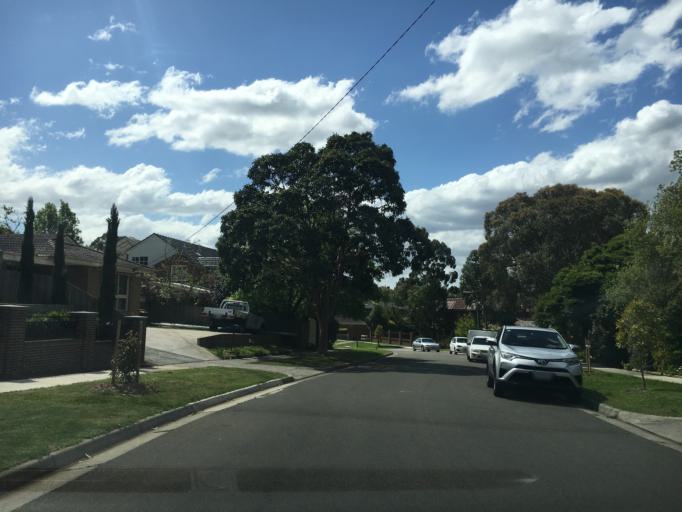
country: AU
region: Victoria
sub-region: Whitehorse
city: Vermont South
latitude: -37.8873
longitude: 145.1834
